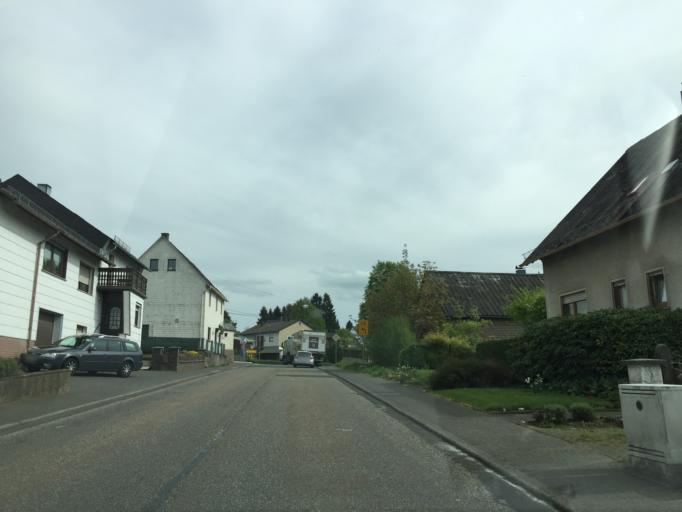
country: DE
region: Rheinland-Pfalz
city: Dreisbach
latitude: 50.6175
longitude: 7.9318
